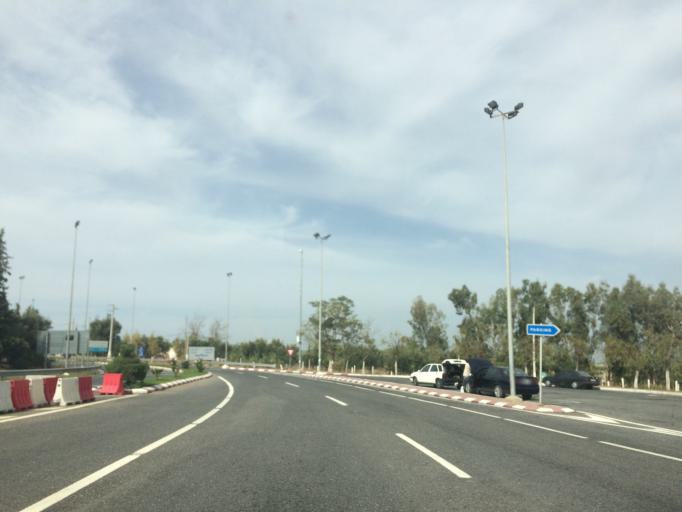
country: MA
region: Meknes-Tafilalet
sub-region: Meknes
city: Meknes
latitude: 33.8335
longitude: -5.5157
